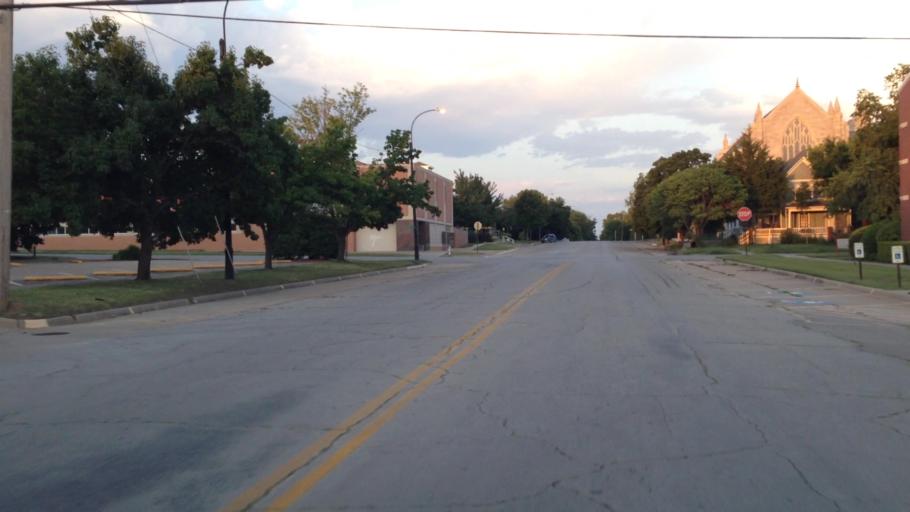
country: US
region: Kansas
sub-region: Montgomery County
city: Independence
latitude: 37.2222
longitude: -95.7062
